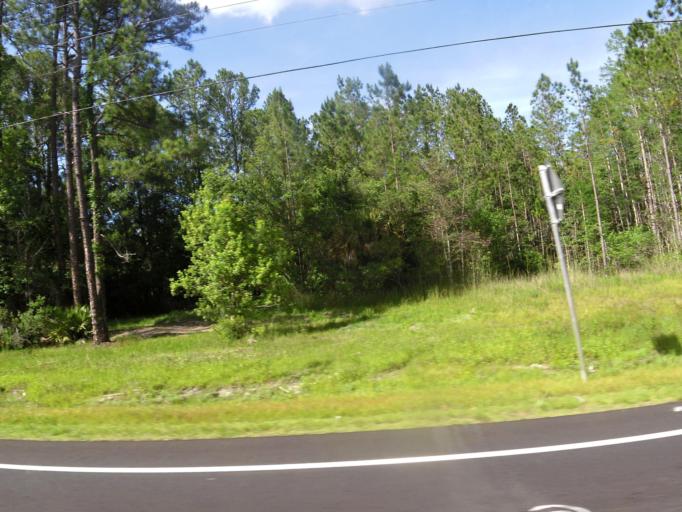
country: US
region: Florida
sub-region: Nassau County
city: Callahan
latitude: 30.5865
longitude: -81.8582
